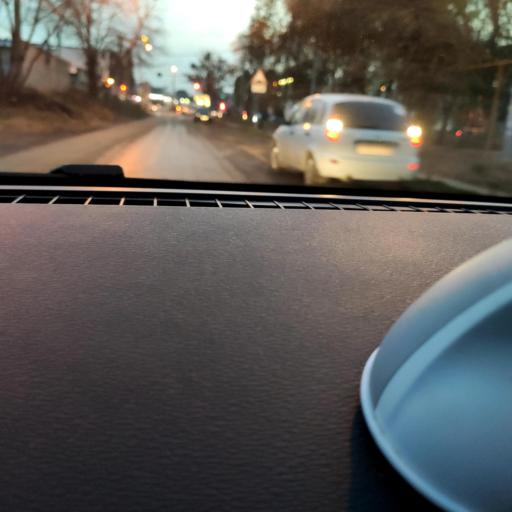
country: RU
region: Samara
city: Samara
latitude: 53.1983
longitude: 50.2479
